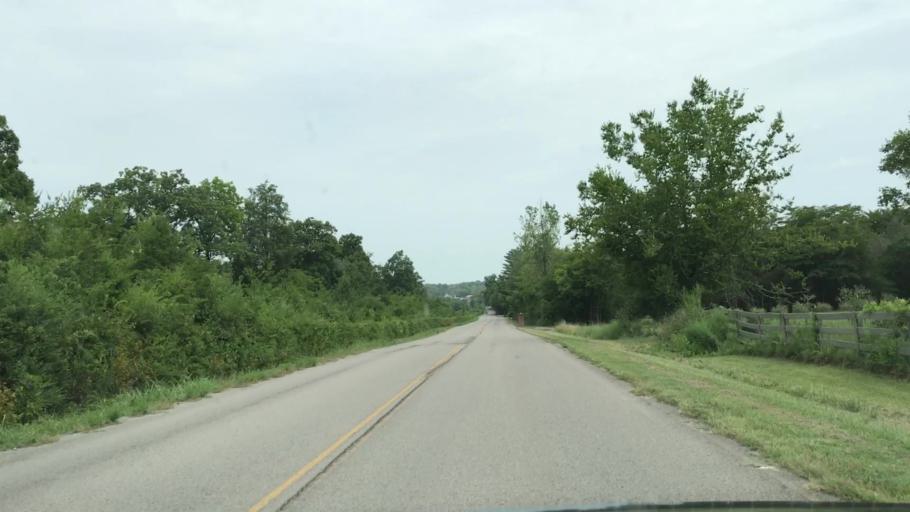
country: US
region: Tennessee
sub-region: Williamson County
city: Nolensville
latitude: 35.9597
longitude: -86.6342
